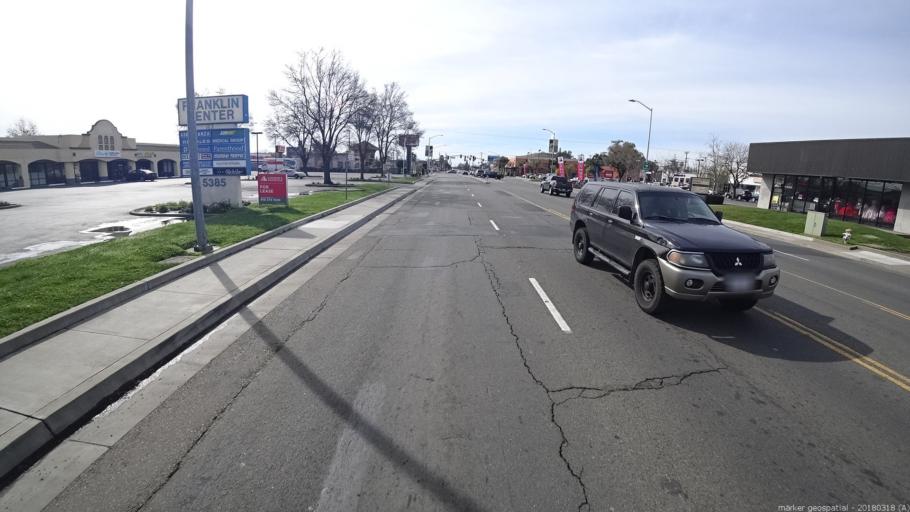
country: US
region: California
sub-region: Sacramento County
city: Parkway
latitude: 38.5263
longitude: -121.4720
